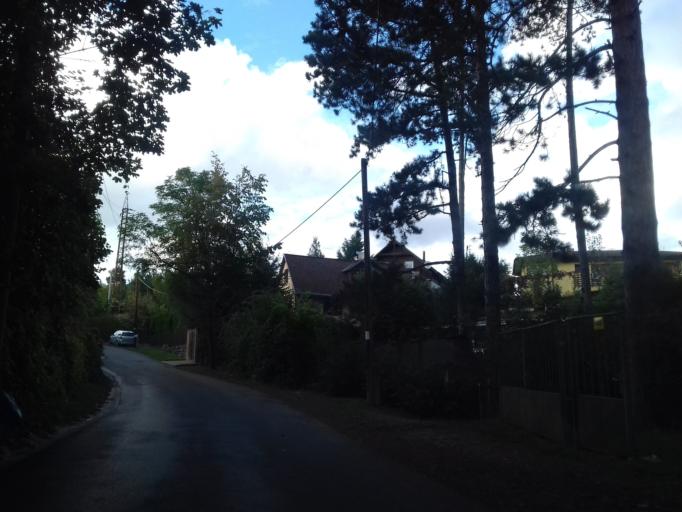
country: CZ
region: Central Bohemia
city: Revnice
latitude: 49.9221
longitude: 14.2389
